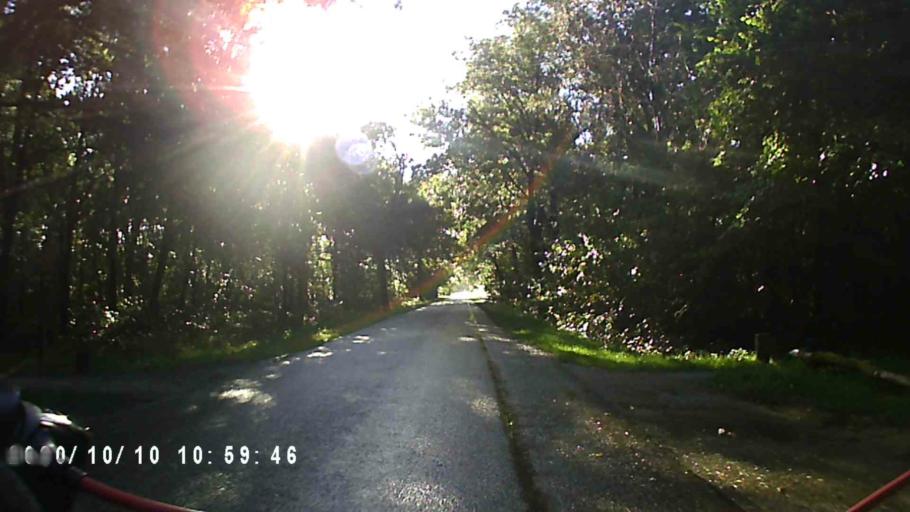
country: NL
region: Friesland
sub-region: Gemeente Achtkarspelen
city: Surhuisterveen
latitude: 53.1412
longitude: 6.2103
